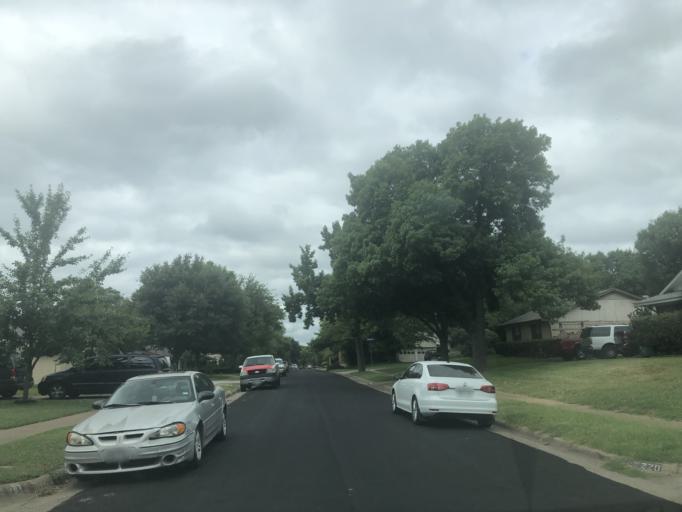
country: US
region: Texas
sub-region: Dallas County
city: Duncanville
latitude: 32.6505
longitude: -96.9123
